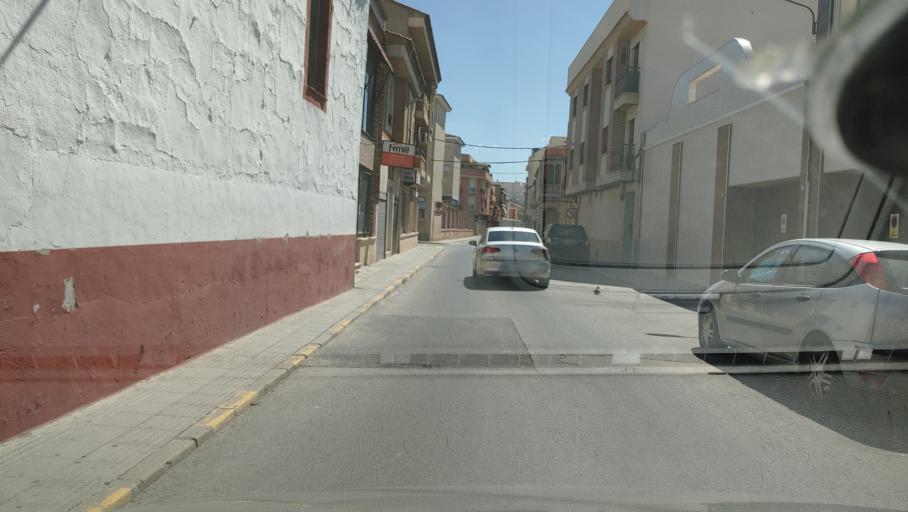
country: ES
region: Castille-La Mancha
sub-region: Provincia de Ciudad Real
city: Valdepenas
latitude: 38.7644
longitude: -3.3825
